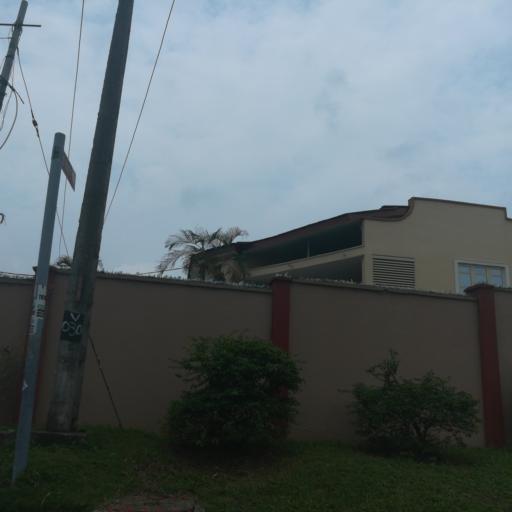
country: NG
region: Lagos
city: Ojota
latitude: 6.5743
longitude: 3.3835
